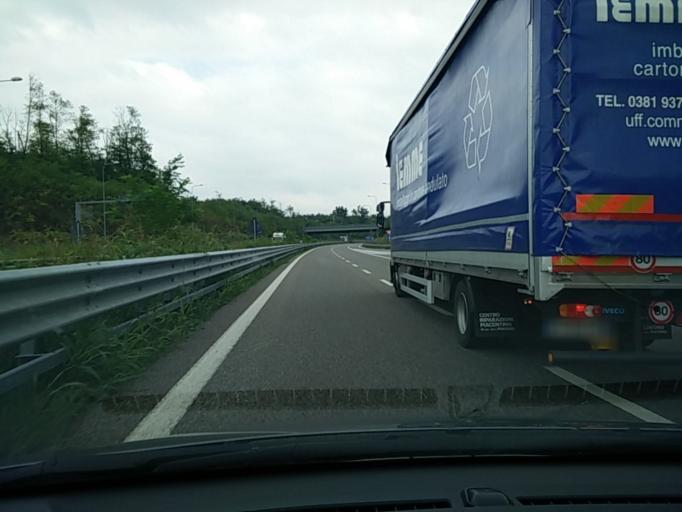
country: IT
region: Lombardy
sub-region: Citta metropolitana di Milano
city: Castano Primo
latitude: 45.5622
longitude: 8.7851
